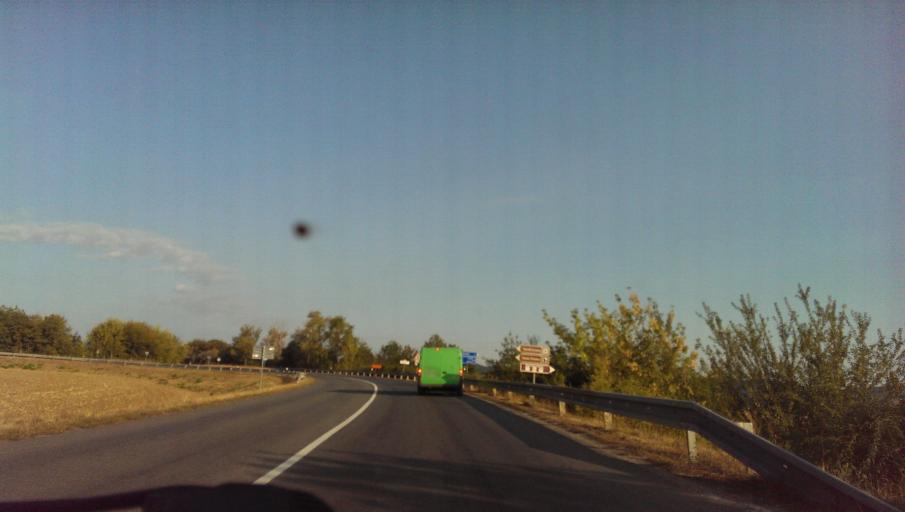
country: CZ
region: Zlin
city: Tupesy
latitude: 49.0745
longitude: 17.3637
